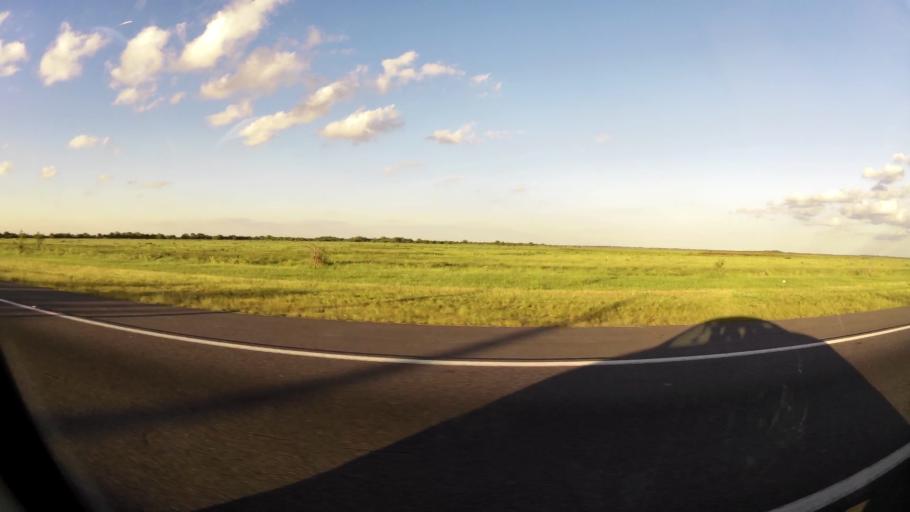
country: AR
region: Buenos Aires
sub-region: Partido de La Plata
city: La Plata
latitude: -34.8226
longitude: -58.1007
